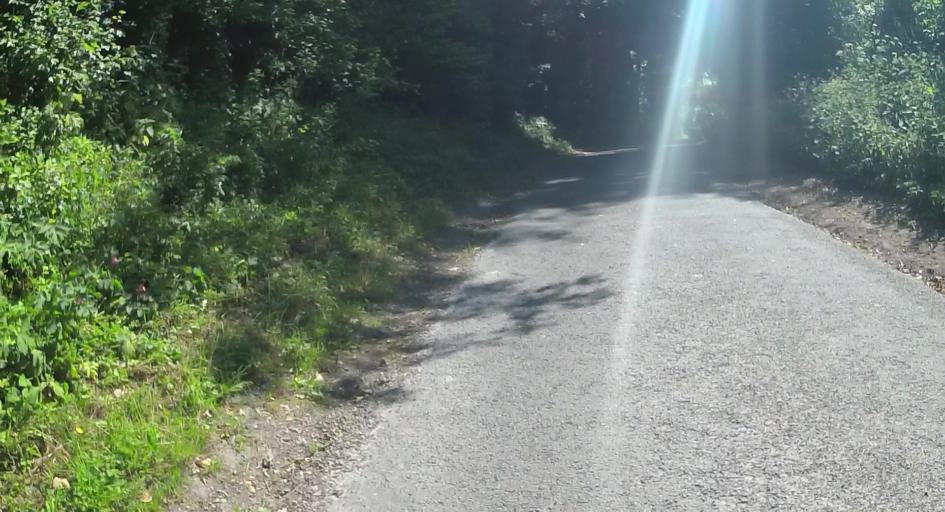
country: GB
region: England
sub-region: Hampshire
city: Kingsclere
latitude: 51.3111
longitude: -1.2944
